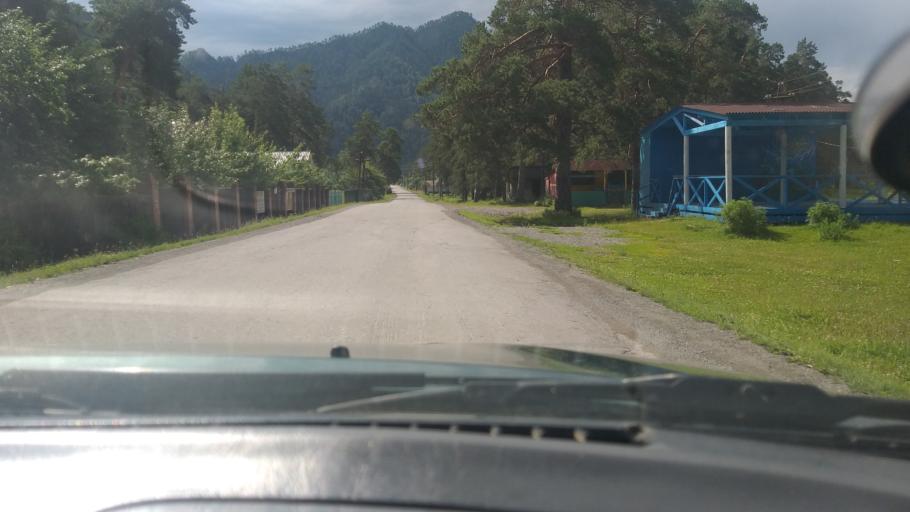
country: RU
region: Altay
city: Chemal
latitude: 51.3981
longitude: 86.0234
